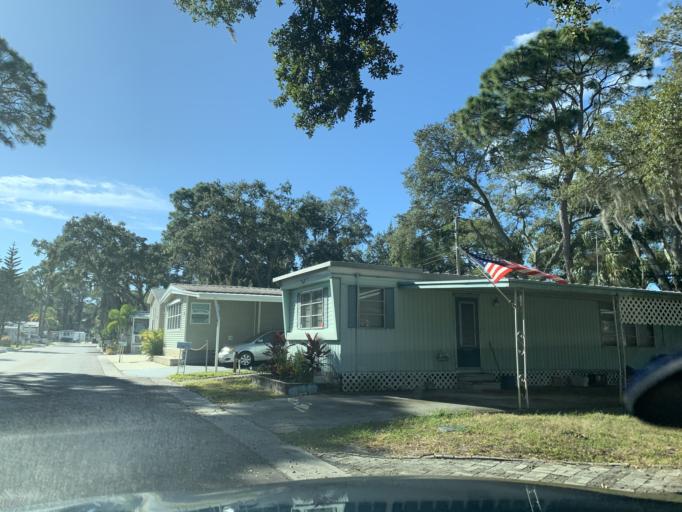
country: US
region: Florida
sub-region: Pinellas County
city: Kenneth City
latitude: 27.8172
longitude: -82.7453
